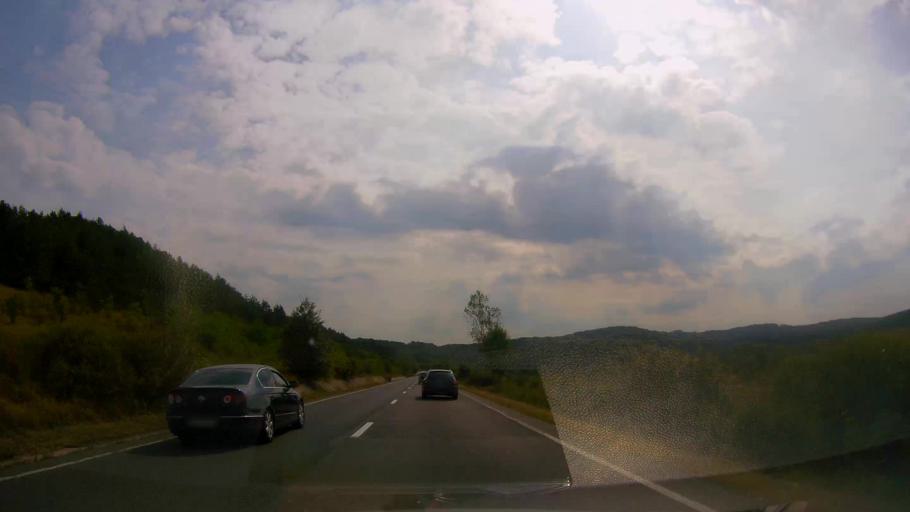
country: RO
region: Salaj
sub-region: Comuna Dragu
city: Dragu
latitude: 46.9484
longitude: 23.3638
